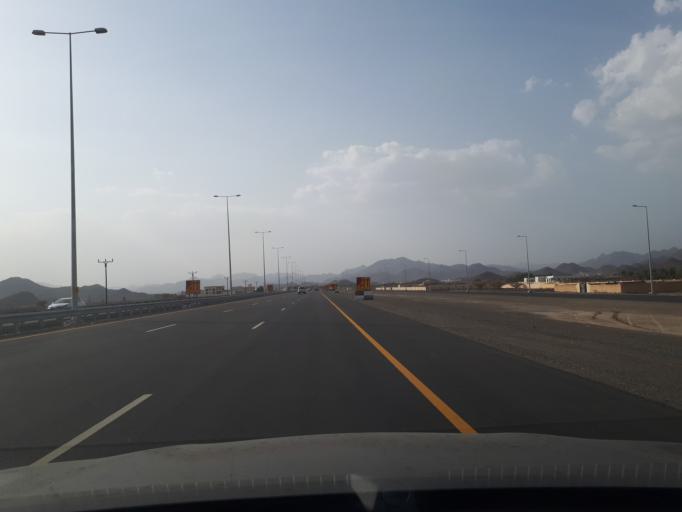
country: OM
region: Ash Sharqiyah
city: Ibra'
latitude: 22.8181
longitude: 58.4370
